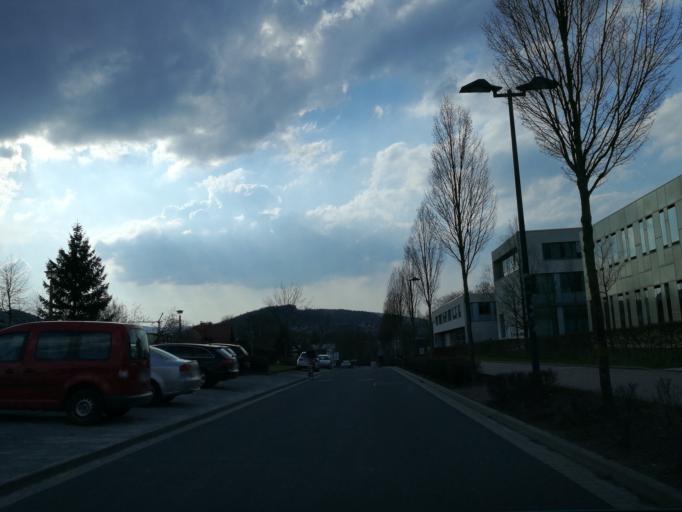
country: DE
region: Thuringia
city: Neuhaus
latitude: 50.6833
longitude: 10.9324
